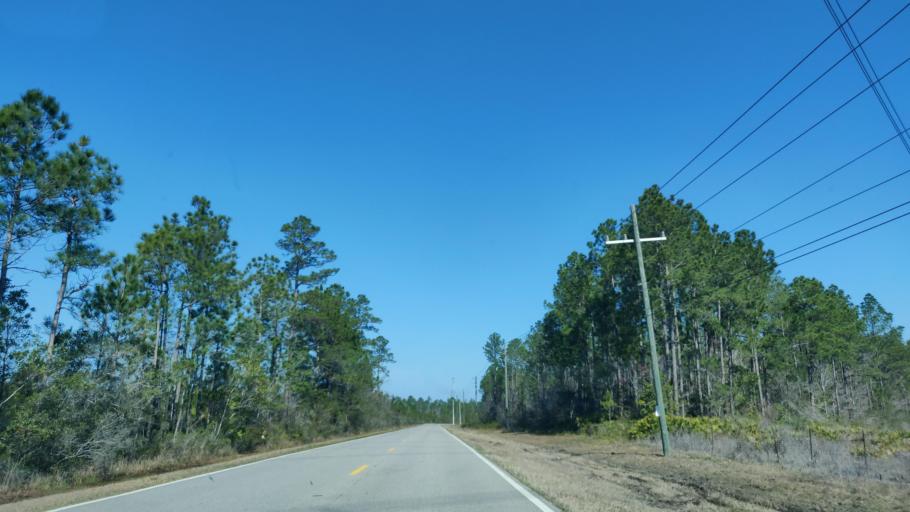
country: US
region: Florida
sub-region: Duval County
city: Baldwin
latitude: 30.2626
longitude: -81.9545
